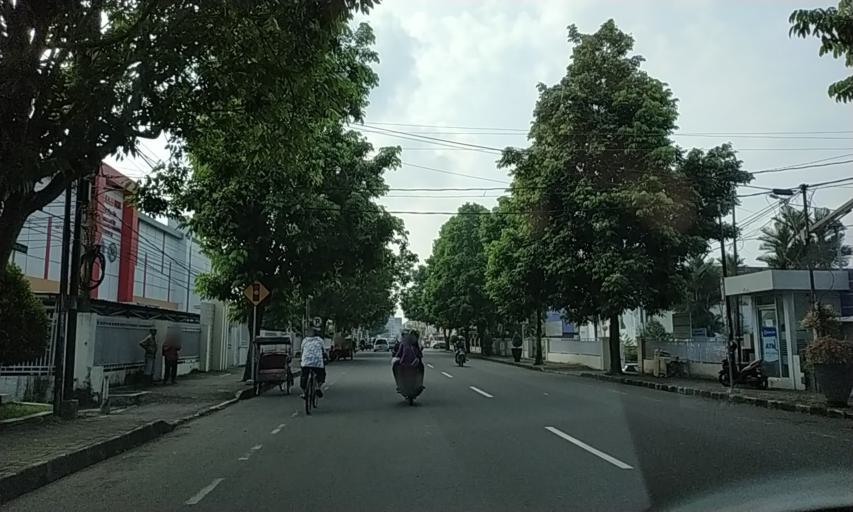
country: ID
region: Central Java
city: Purwokerto
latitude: -7.4226
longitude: 109.2415
